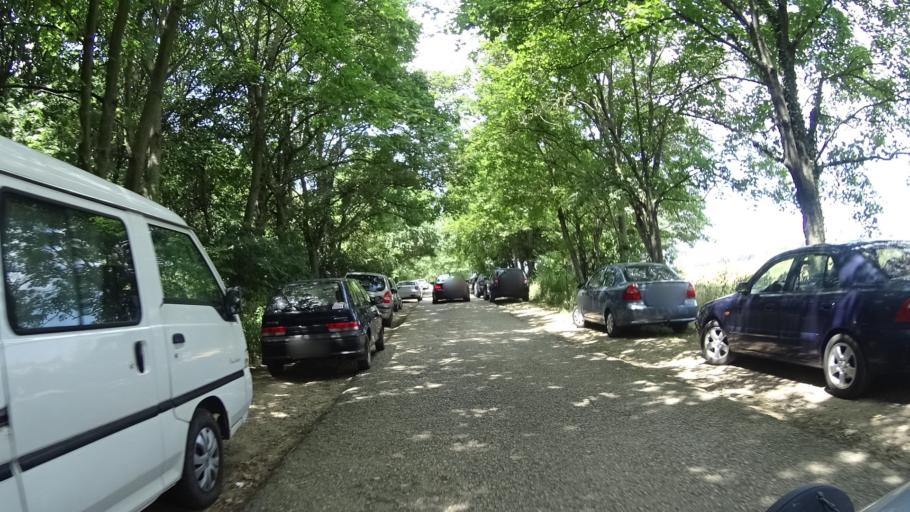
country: HU
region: Veszprem
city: Veszprem
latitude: 47.0887
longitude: 17.8955
